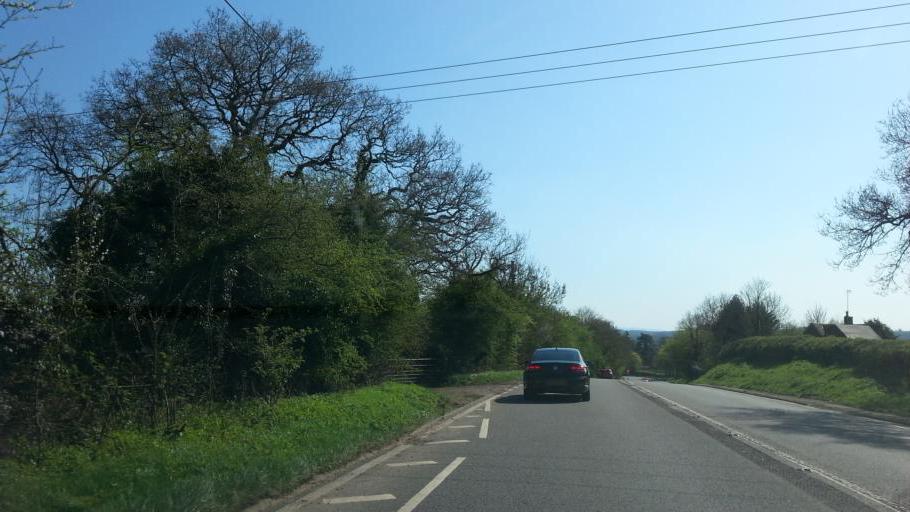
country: GB
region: England
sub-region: Worcestershire
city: Alvechurch
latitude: 52.3812
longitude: -1.9579
